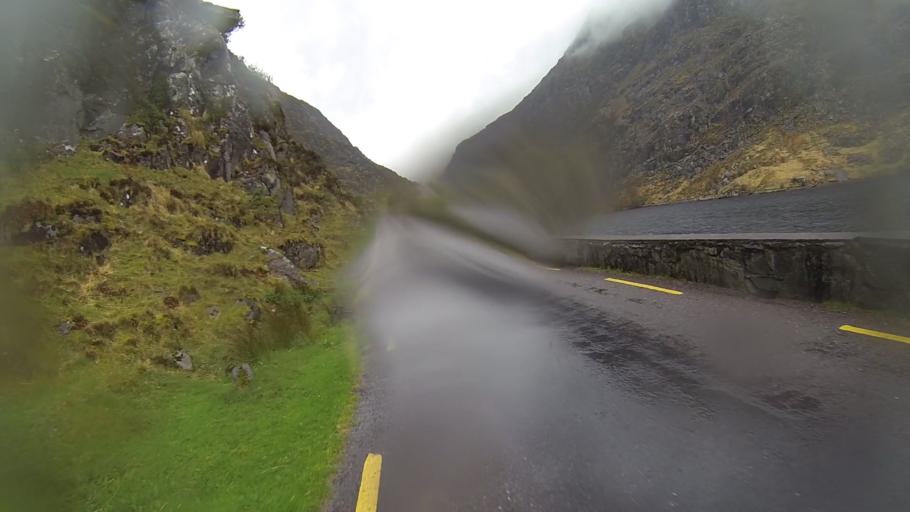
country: IE
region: Munster
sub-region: Ciarrai
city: Cill Airne
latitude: 52.0130
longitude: -9.6364
